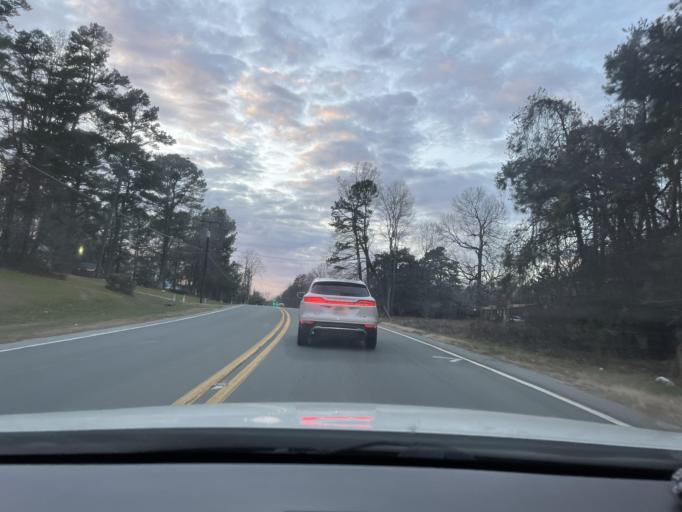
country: US
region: North Carolina
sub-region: Guilford County
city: McLeansville
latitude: 36.0664
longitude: -79.6156
